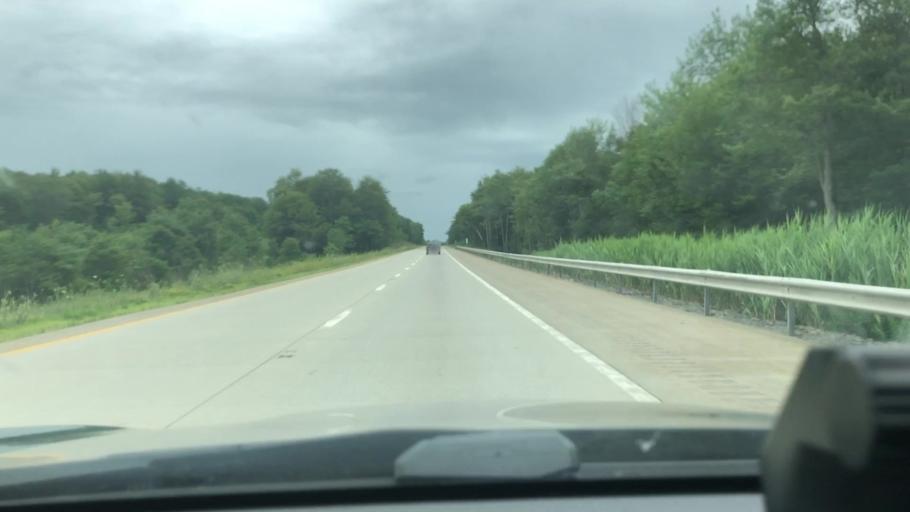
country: US
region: Pennsylvania
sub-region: Monroe County
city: Mount Pocono
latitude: 41.1526
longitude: -75.4112
